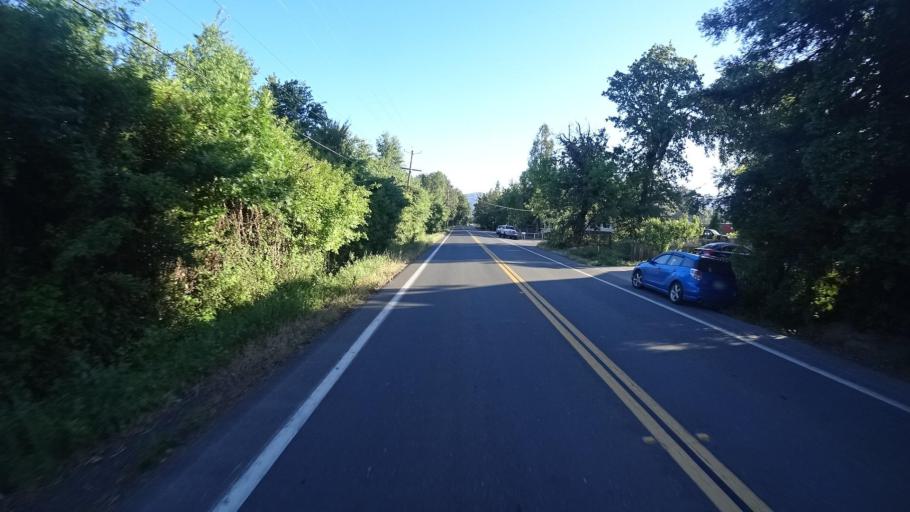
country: US
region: California
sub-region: Lake County
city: Upper Lake
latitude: 39.1639
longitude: -122.9125
